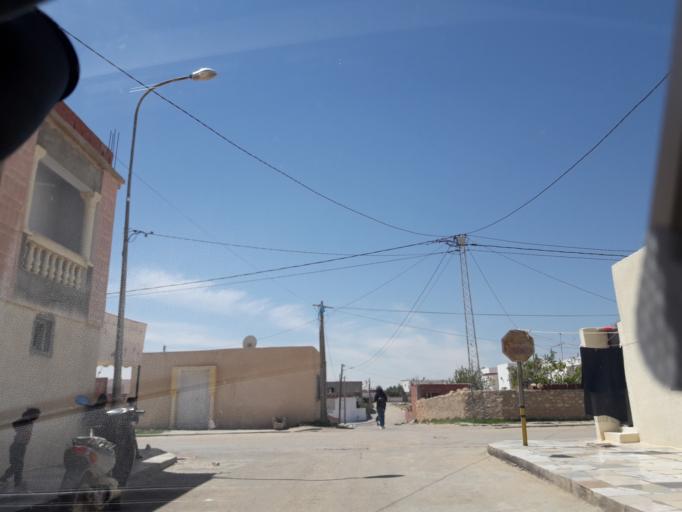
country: TN
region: Safaqis
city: Sfax
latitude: 34.7392
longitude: 10.5221
